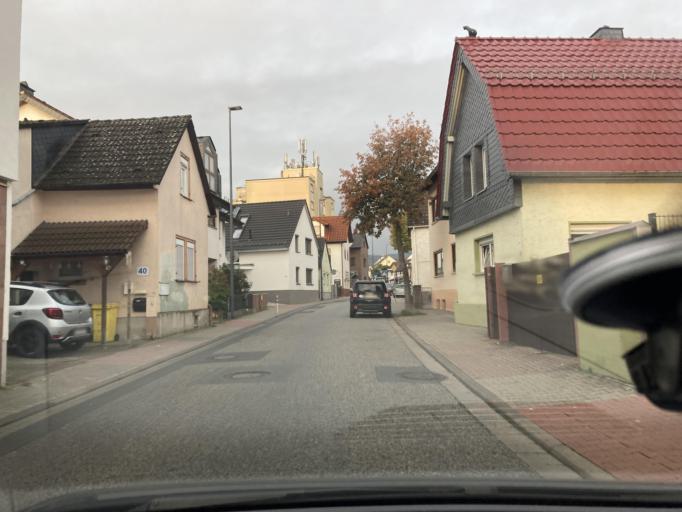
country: DE
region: Hesse
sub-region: Regierungsbezirk Darmstadt
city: Oberursel
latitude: 50.2266
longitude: 8.5757
